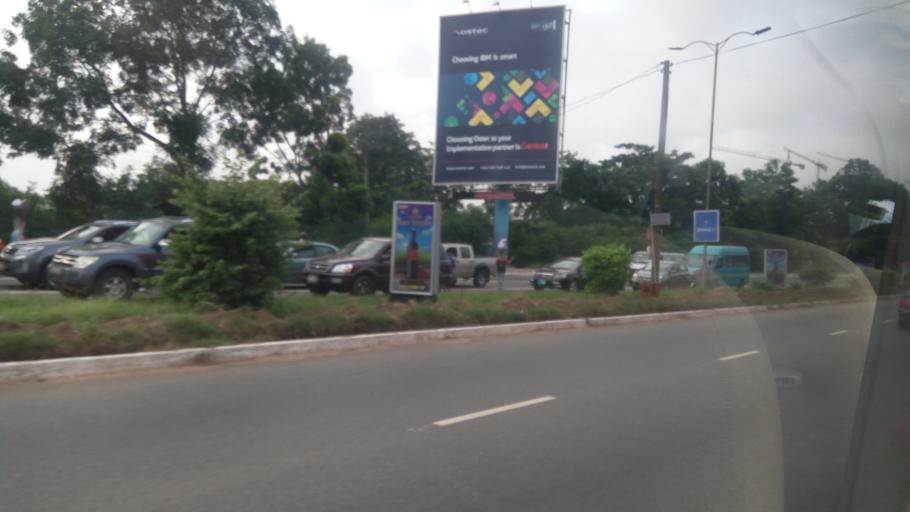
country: GH
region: Greater Accra
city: Medina Estates
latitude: 5.6141
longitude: -0.1761
